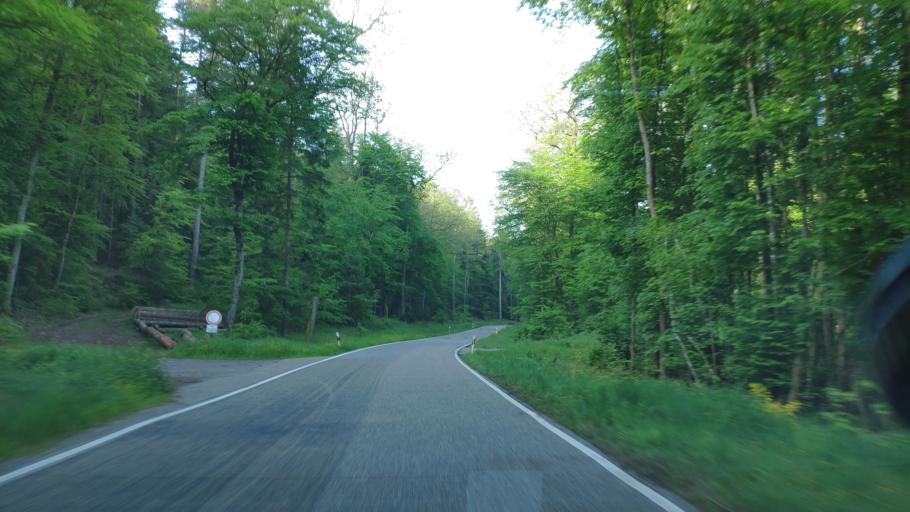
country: DE
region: Rheinland-Pfalz
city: Ruppertsweiler
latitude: 49.1568
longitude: 7.7127
